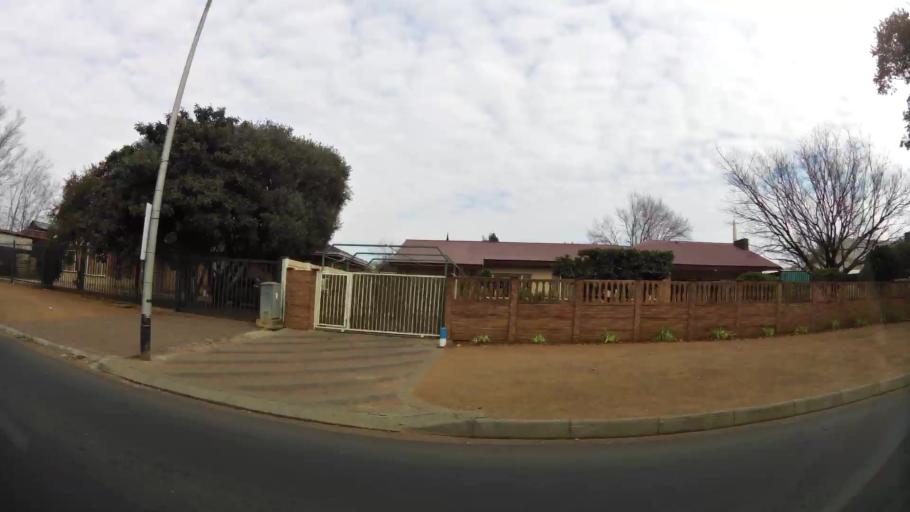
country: ZA
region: Orange Free State
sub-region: Mangaung Metropolitan Municipality
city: Bloemfontein
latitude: -29.1273
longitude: 26.1776
